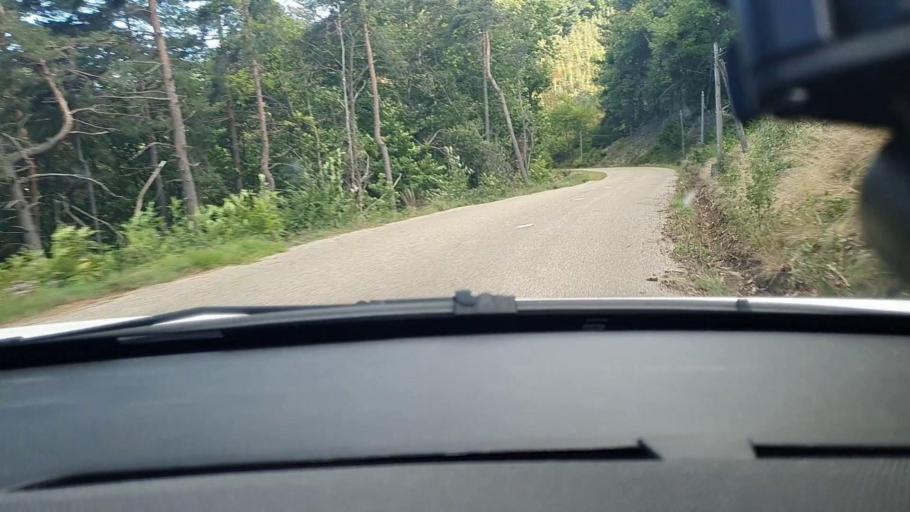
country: FR
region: Rhone-Alpes
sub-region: Departement de l'Ardeche
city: Les Vans
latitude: 44.4223
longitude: 4.0227
